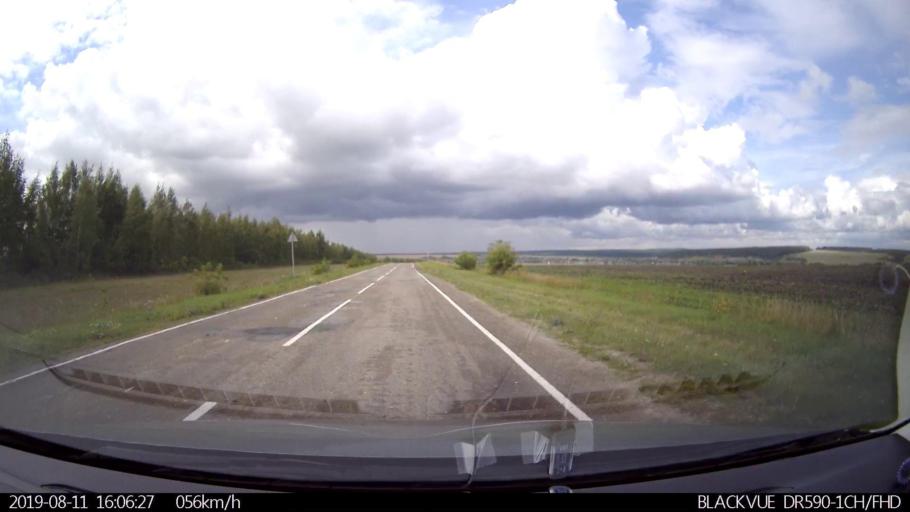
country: RU
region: Ulyanovsk
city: Ignatovka
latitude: 53.9690
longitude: 47.6485
